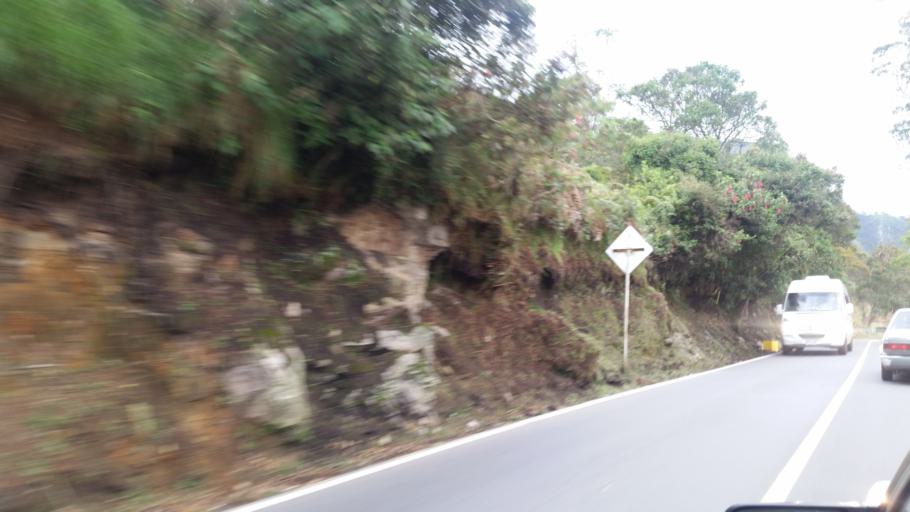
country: CO
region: Cundinamarca
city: Choachi
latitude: 4.5573
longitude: -73.9509
